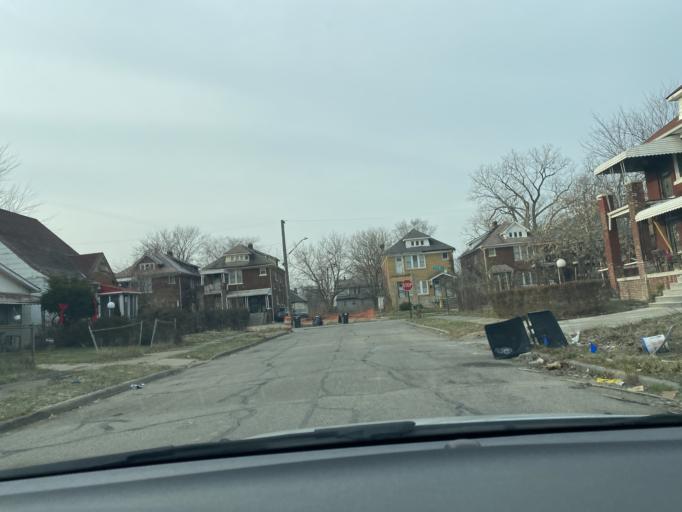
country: US
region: Michigan
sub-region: Wayne County
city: Highland Park
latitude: 42.3802
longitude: -83.1315
